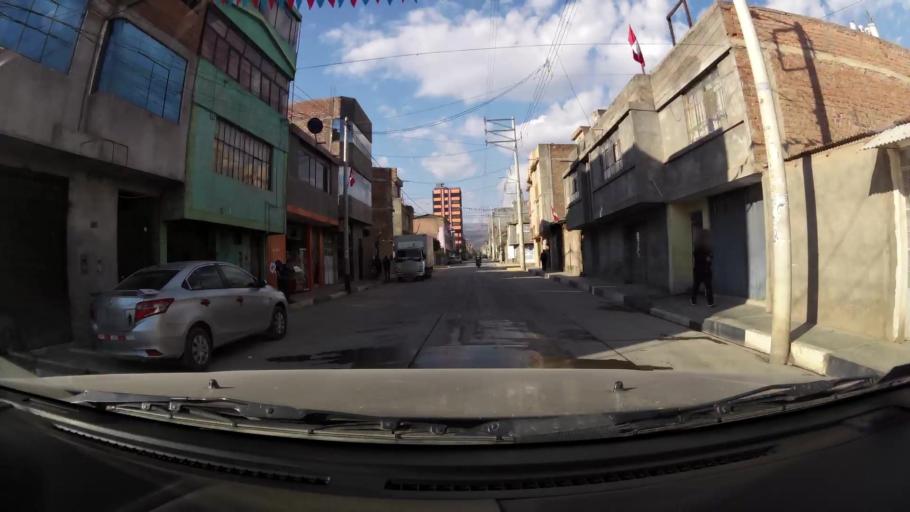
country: PE
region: Junin
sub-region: Provincia de Huancayo
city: El Tambo
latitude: -12.0560
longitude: -75.2253
